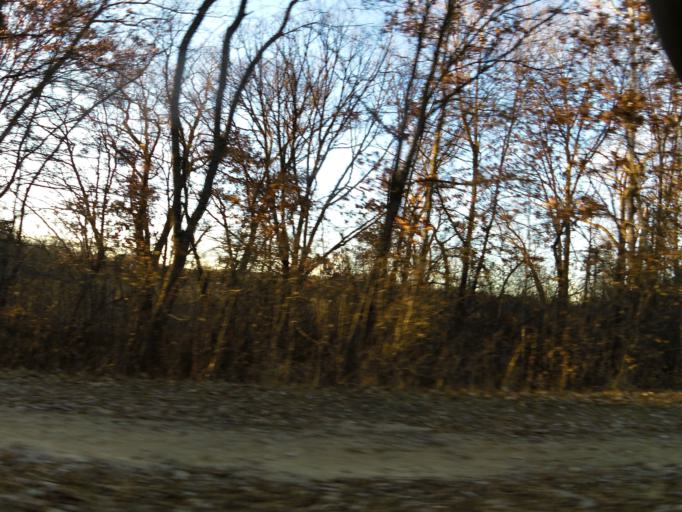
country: US
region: Minnesota
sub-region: Washington County
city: Grant
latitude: 45.0977
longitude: -92.8734
